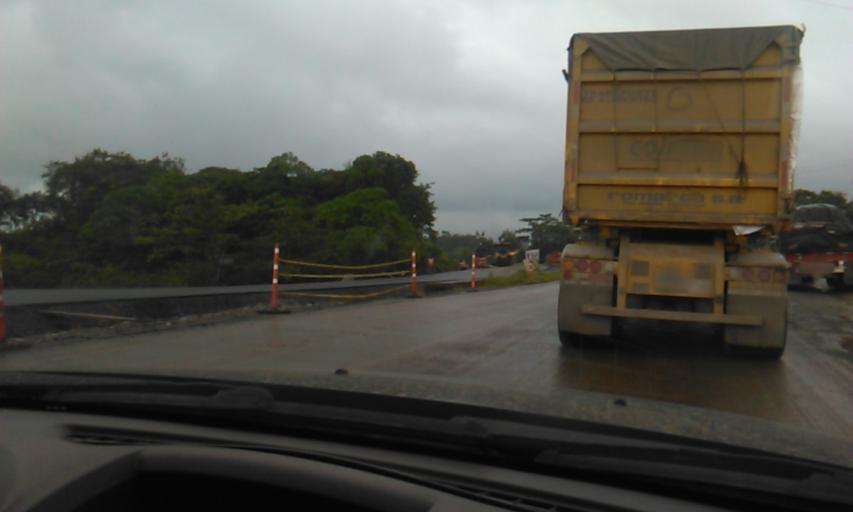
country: CO
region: Valle del Cauca
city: Buenaventura
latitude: 3.8784
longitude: -76.8965
